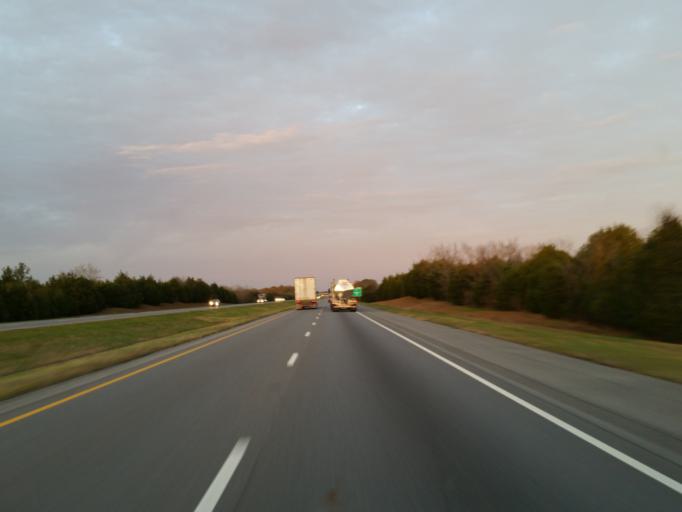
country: US
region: Alabama
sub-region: Sumter County
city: Livingston
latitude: 32.6850
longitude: -88.1595
